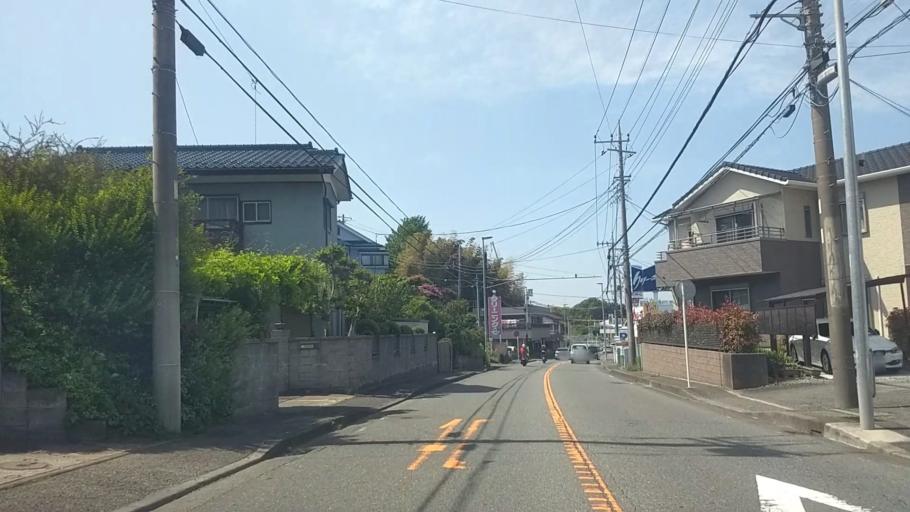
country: JP
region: Kanagawa
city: Kamakura
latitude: 35.3501
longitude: 139.5808
